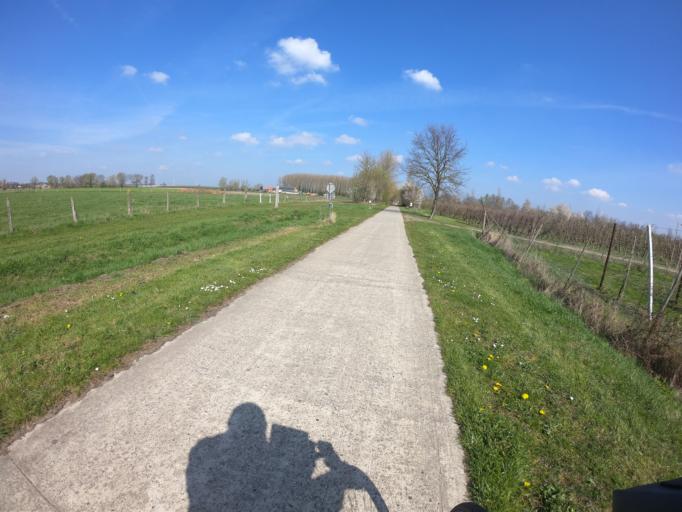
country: BE
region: Flanders
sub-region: Provincie Vlaams-Brabant
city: Geetbets
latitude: 50.9140
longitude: 5.1122
